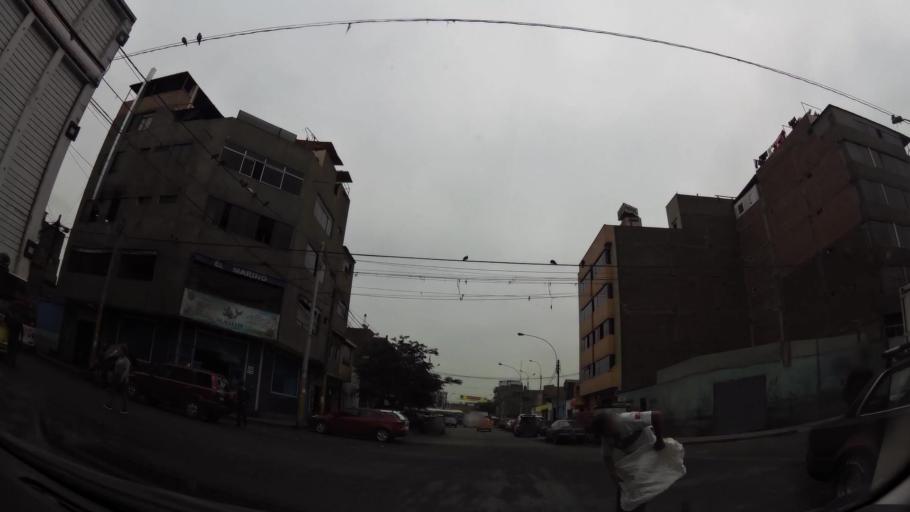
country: PE
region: Lima
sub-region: Lima
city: San Luis
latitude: -12.0699
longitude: -77.0100
